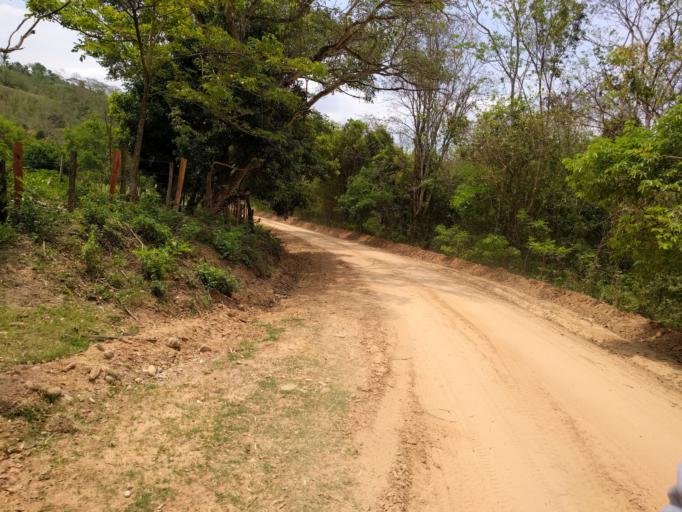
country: BO
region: Santa Cruz
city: Santa Rita
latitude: -17.9335
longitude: -63.3716
